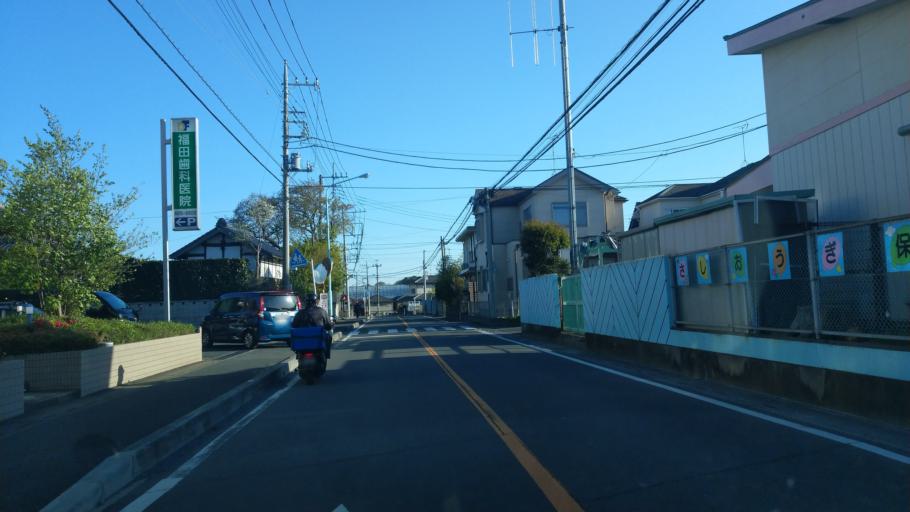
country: JP
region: Saitama
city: Ageoshimo
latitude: 35.9275
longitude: 139.5711
